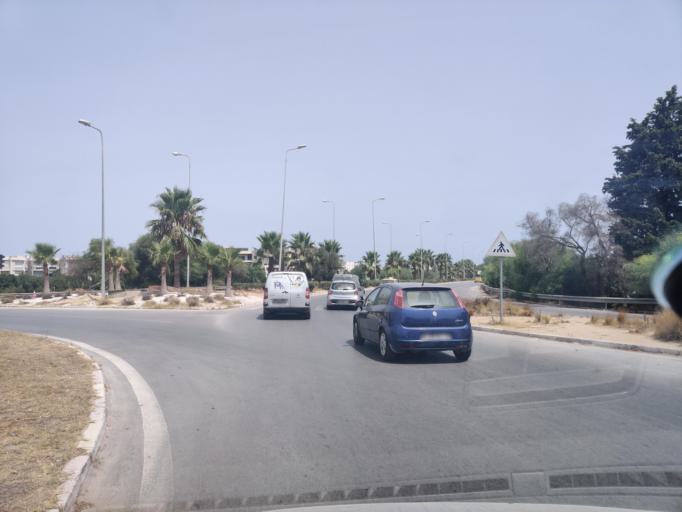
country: TN
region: Tunis
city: Carthage
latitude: 36.8587
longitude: 10.3132
